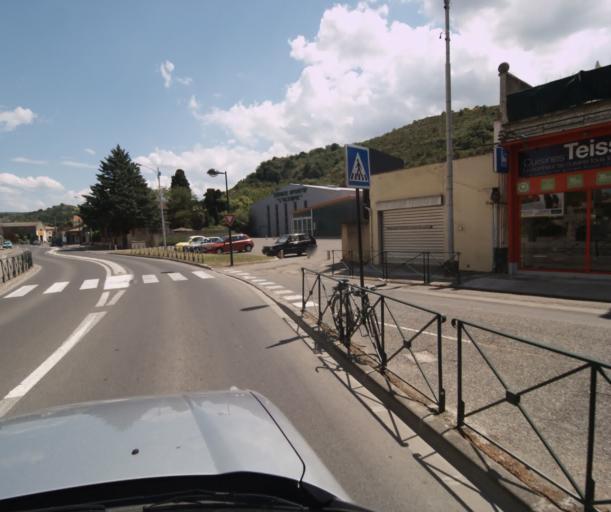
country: FR
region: Languedoc-Roussillon
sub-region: Departement de l'Aude
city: Limoux
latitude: 43.0505
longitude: 2.2185
